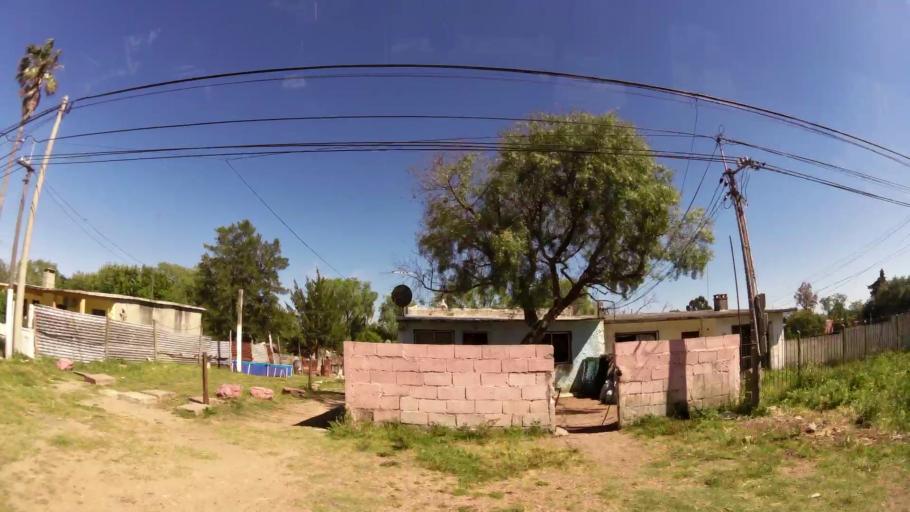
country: UY
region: Canelones
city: Paso de Carrasco
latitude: -34.8624
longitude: -56.1138
